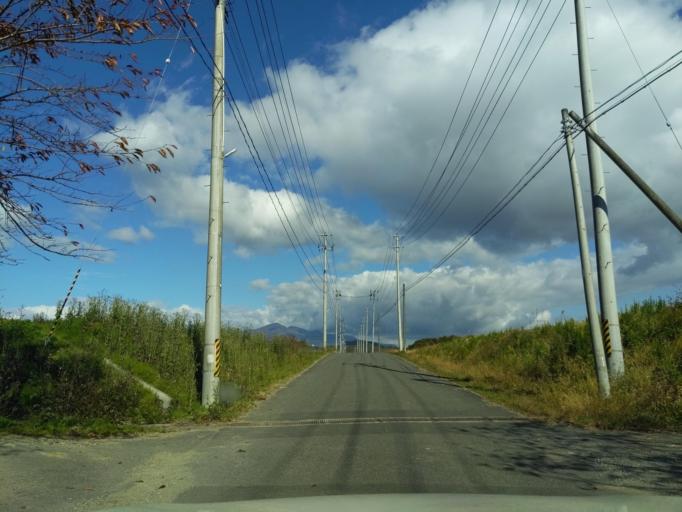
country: JP
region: Fukushima
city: Koriyama
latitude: 37.4517
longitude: 140.3206
